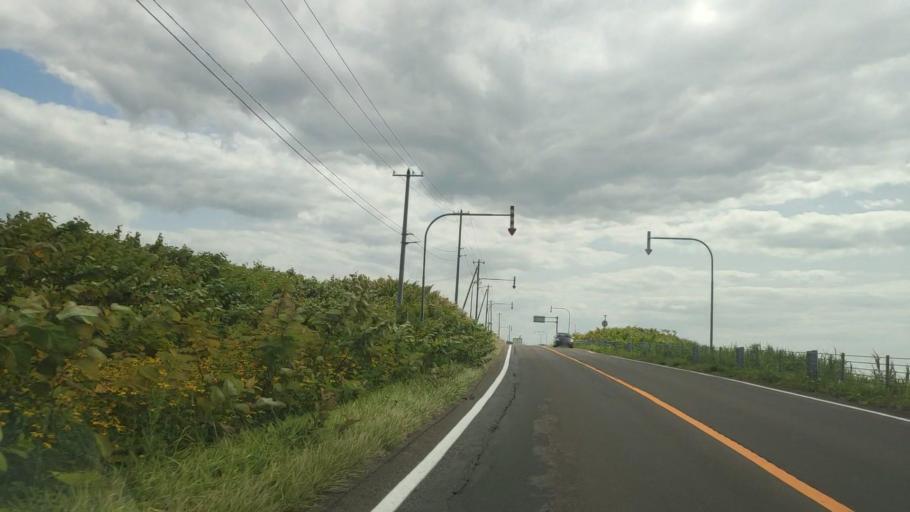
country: JP
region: Hokkaido
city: Rumoi
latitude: 44.5393
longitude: 141.7663
